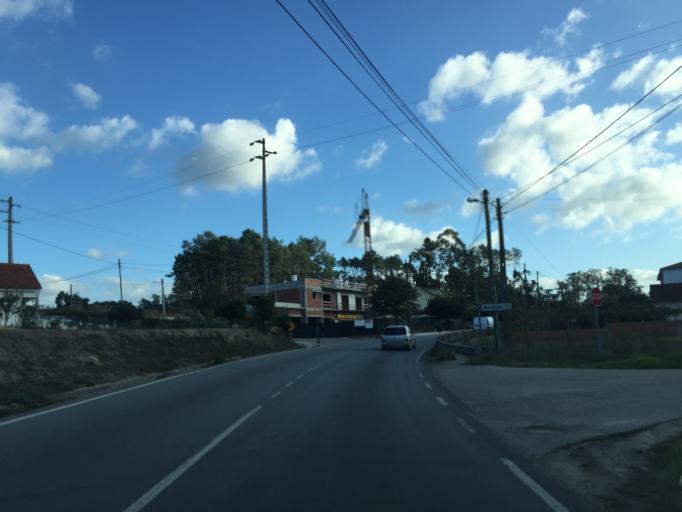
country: PT
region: Leiria
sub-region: Leiria
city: Souto da Carpalhosa
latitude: 39.8588
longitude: -8.8354
